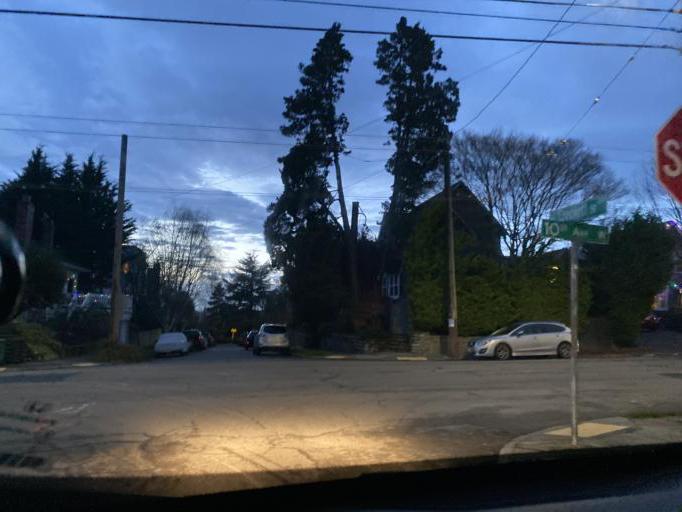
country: US
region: Washington
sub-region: King County
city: Seattle
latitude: 47.6378
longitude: -122.3701
